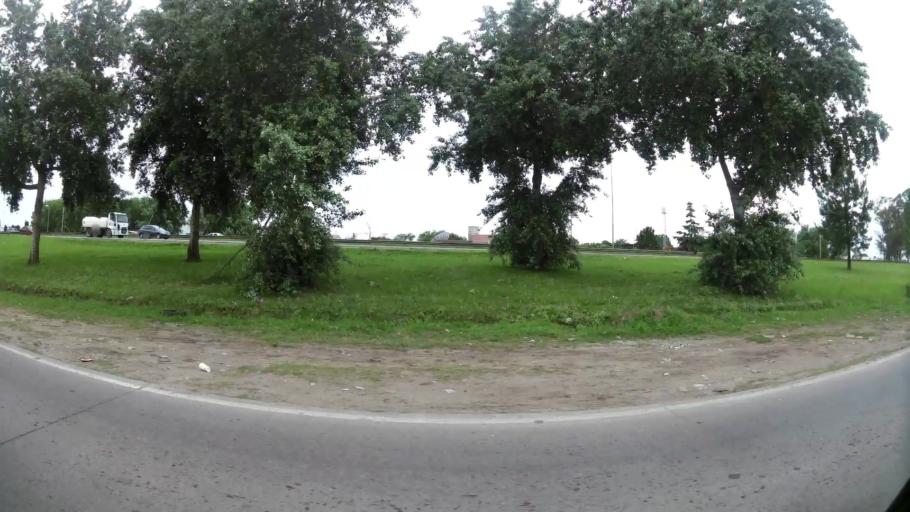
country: AR
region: Buenos Aires
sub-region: Partido de Campana
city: Campana
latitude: -34.1931
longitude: -58.9430
